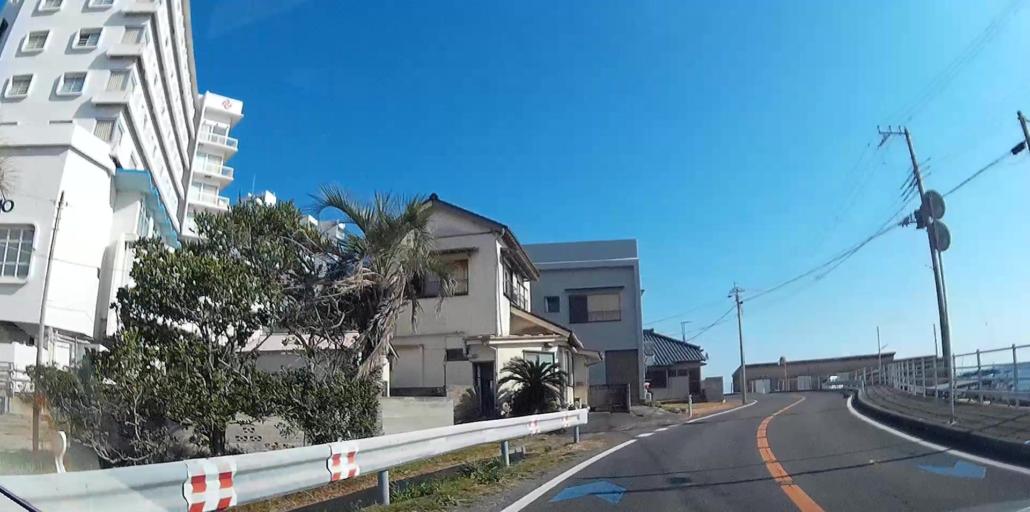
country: JP
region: Chiba
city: Tateyama
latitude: 34.9063
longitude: 139.8989
